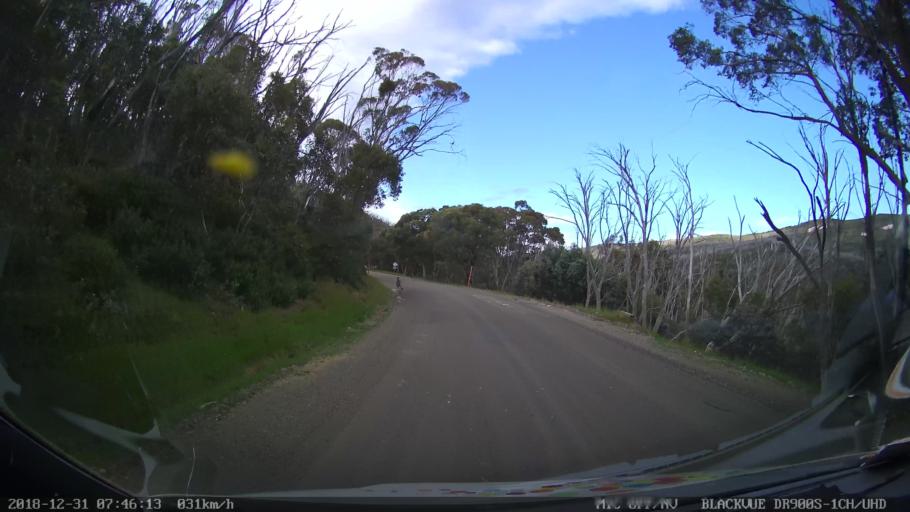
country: AU
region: New South Wales
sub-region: Snowy River
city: Jindabyne
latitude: -36.3610
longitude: 148.4019
